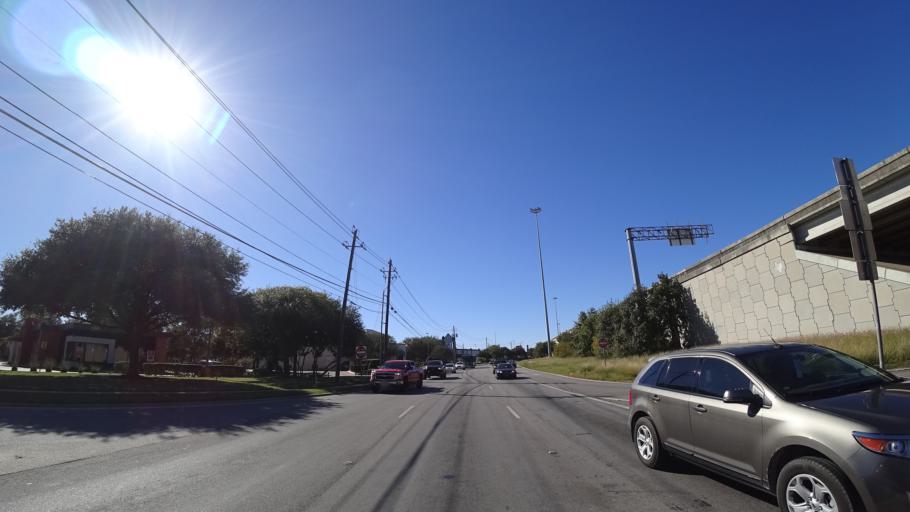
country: US
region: Texas
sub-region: Travis County
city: Rollingwood
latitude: 30.2326
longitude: -97.8187
